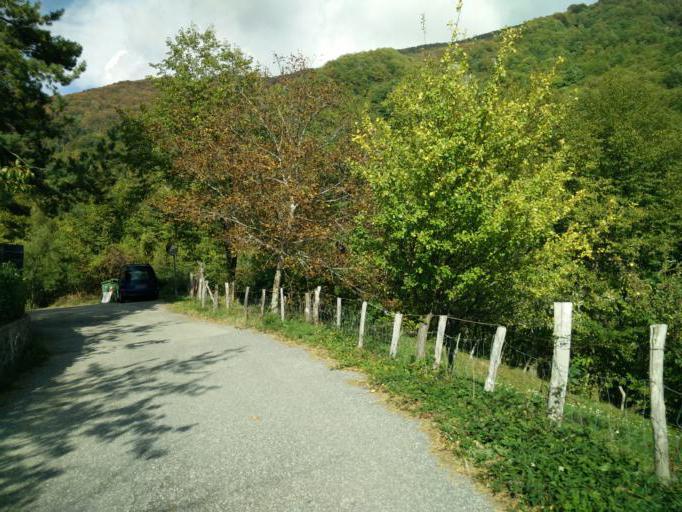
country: IT
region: Tuscany
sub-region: Provincia di Massa-Carrara
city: Patigno
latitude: 44.3588
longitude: 9.7247
